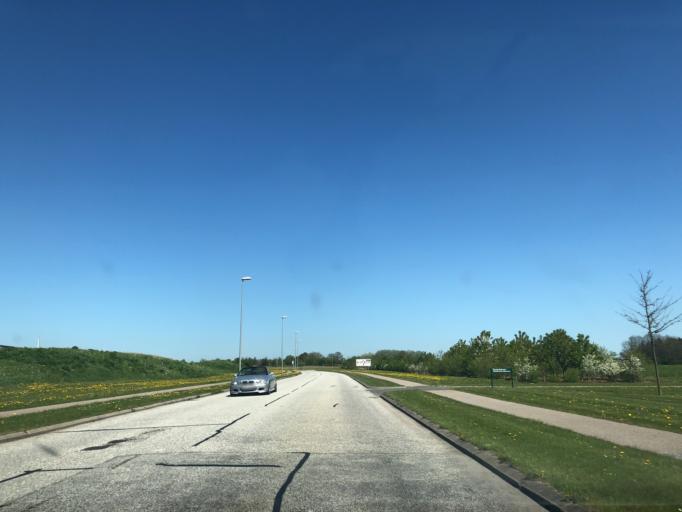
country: DK
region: Zealand
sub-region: Ringsted Kommune
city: Ringsted
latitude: 55.4618
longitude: 11.8217
